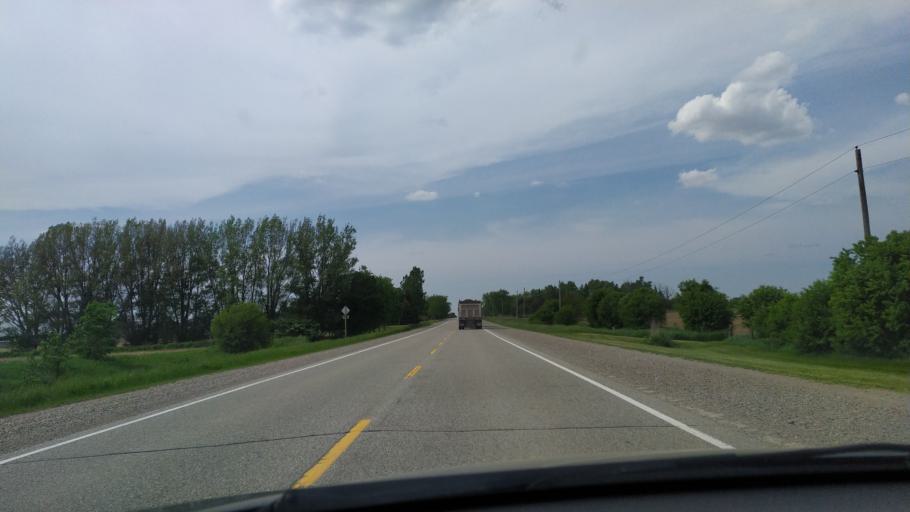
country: CA
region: Ontario
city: Stratford
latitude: 43.2245
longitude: -81.0732
